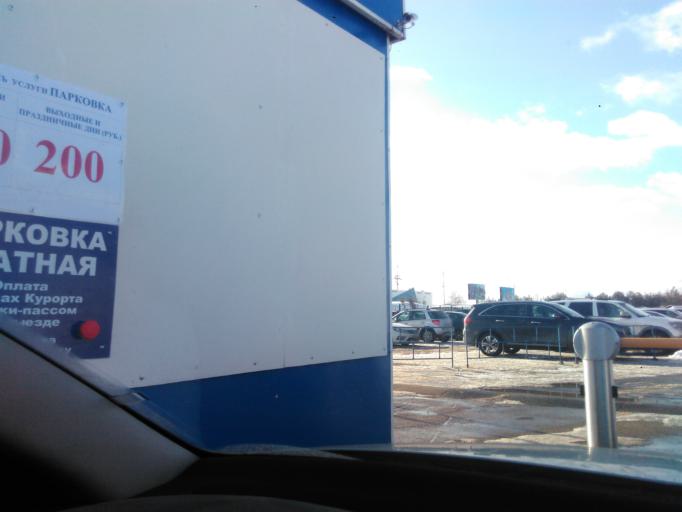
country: RU
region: Moskovskaya
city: Dedenevo
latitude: 56.2790
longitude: 37.5672
